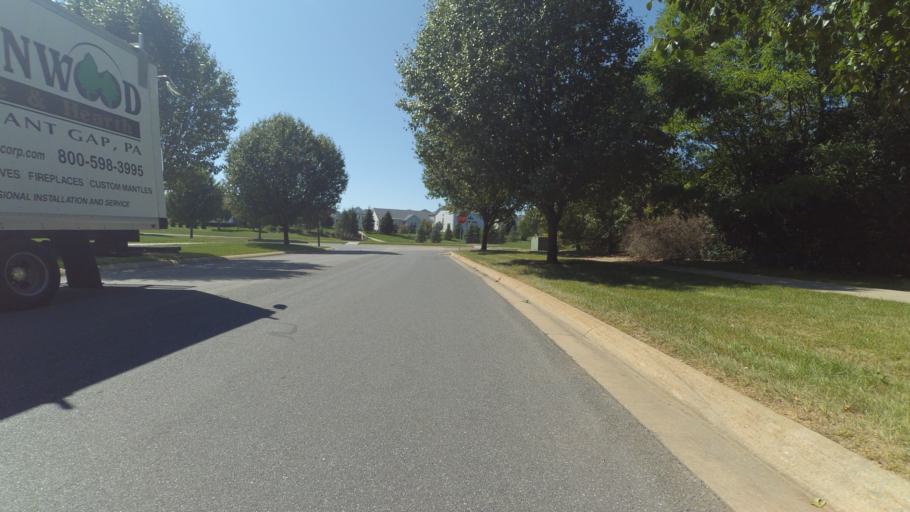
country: US
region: Pennsylvania
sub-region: Centre County
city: Pine Grove Mills
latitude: 40.7715
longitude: -77.8941
